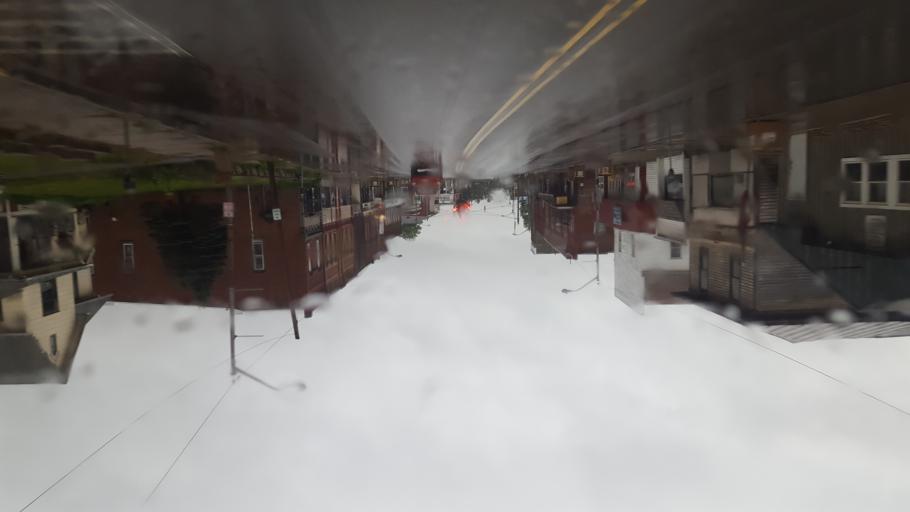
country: US
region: Pennsylvania
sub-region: Tioga County
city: Westfield
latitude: 41.9189
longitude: -77.5410
